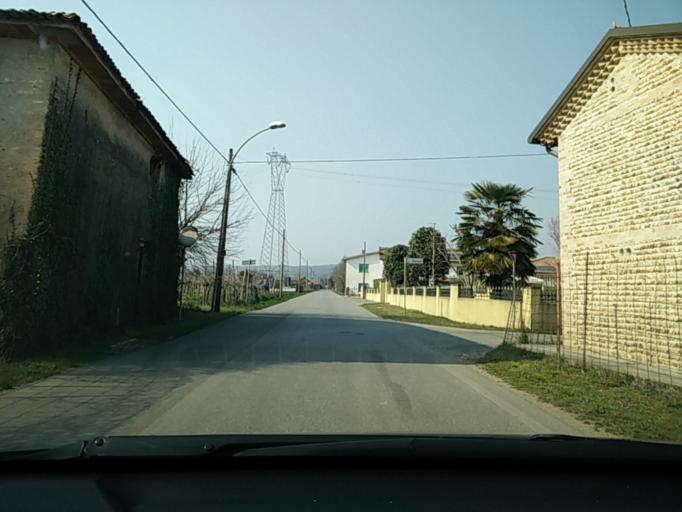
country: IT
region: Veneto
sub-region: Provincia di Treviso
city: Falze-Signoressa
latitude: 45.7618
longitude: 12.1160
